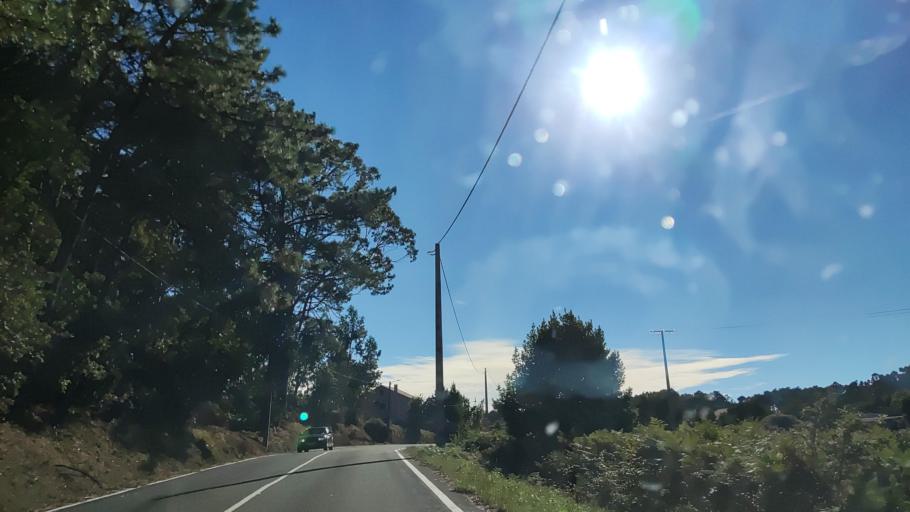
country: ES
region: Galicia
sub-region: Provincia da Coruna
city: Boiro
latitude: 42.5716
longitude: -9.0163
